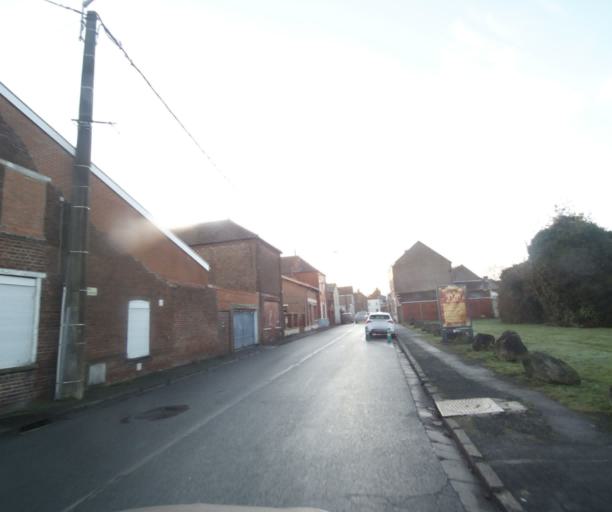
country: FR
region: Nord-Pas-de-Calais
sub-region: Departement du Nord
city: Onnaing
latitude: 50.3870
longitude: 3.6020
